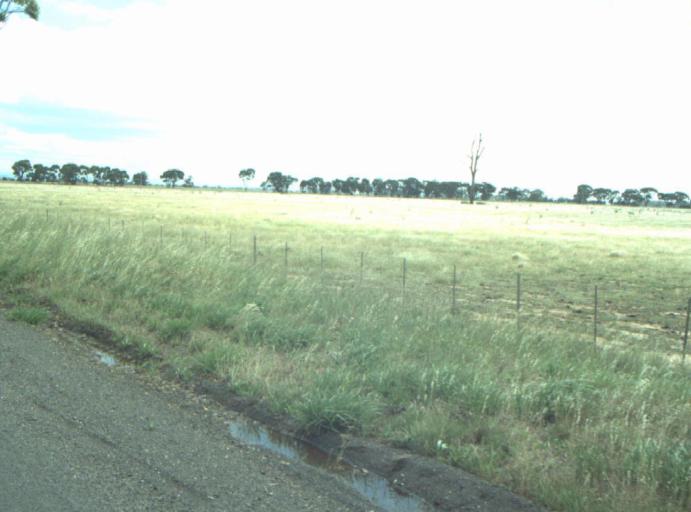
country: AU
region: Victoria
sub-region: Greater Geelong
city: Lara
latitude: -37.8755
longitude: 144.3501
